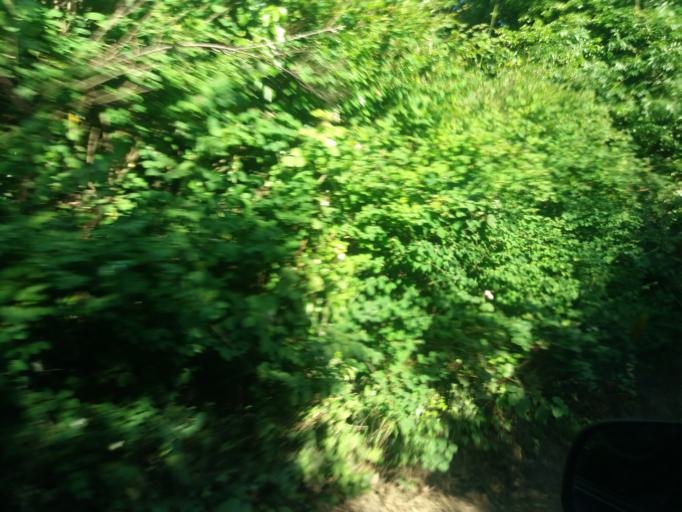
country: IE
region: Leinster
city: Hartstown
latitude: 53.3645
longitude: -6.4087
